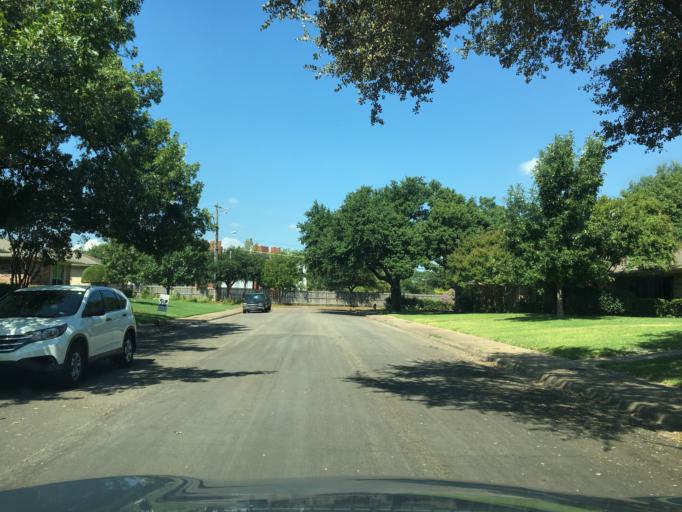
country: US
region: Texas
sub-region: Dallas County
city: Garland
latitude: 32.8635
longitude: -96.6910
